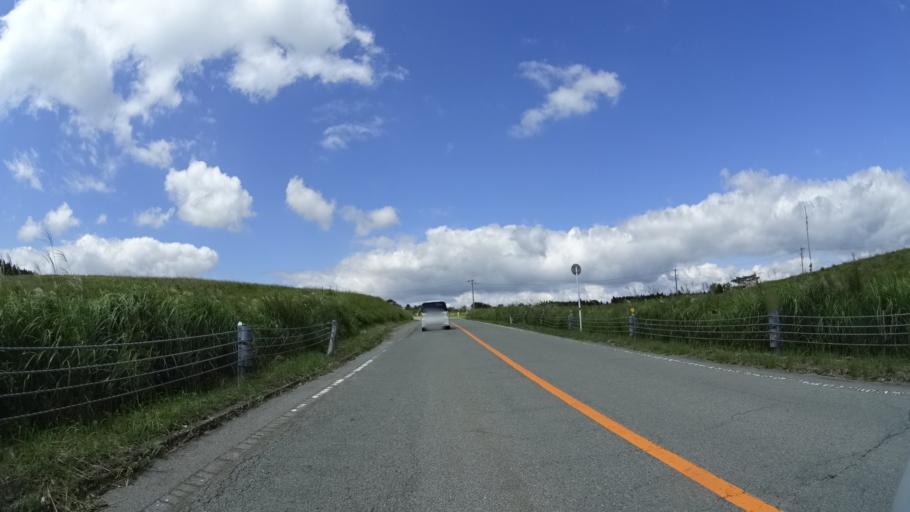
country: JP
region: Kumamoto
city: Aso
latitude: 33.0071
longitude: 131.1226
